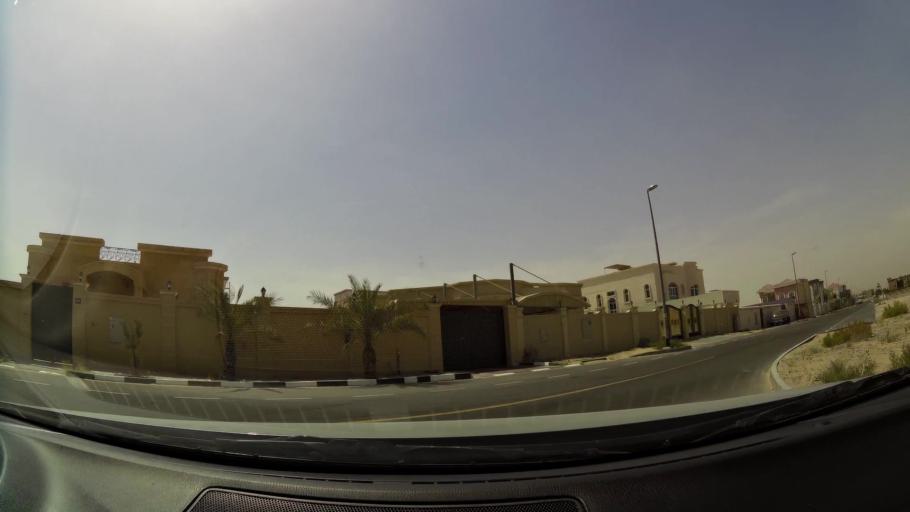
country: AE
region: Ash Shariqah
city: Sharjah
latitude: 25.1867
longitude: 55.4321
